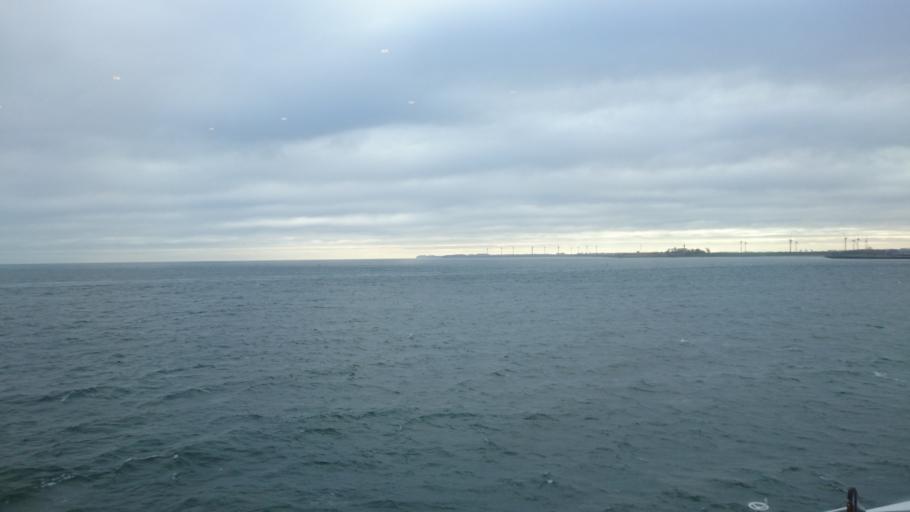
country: DE
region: Schleswig-Holstein
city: Fehmarn
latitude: 54.5170
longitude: 11.2376
